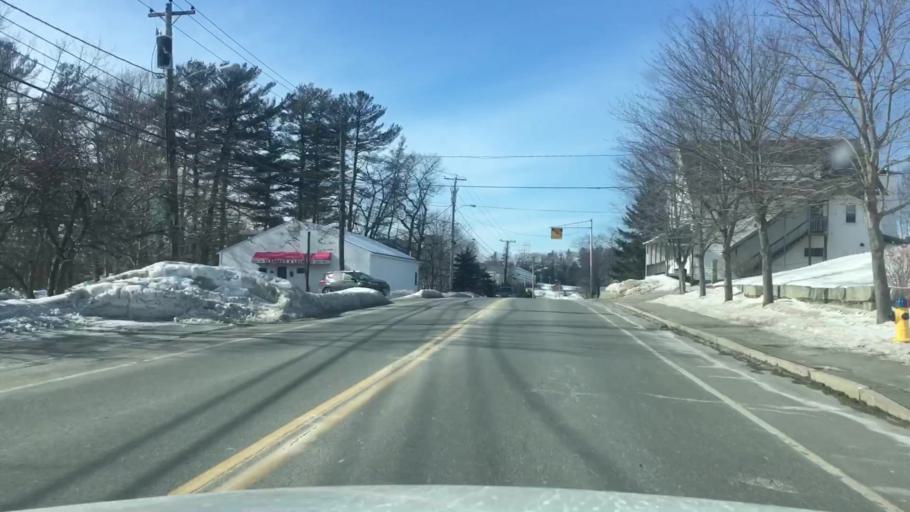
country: US
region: Maine
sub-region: Hancock County
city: Bucksport
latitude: 44.5752
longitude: -68.8015
